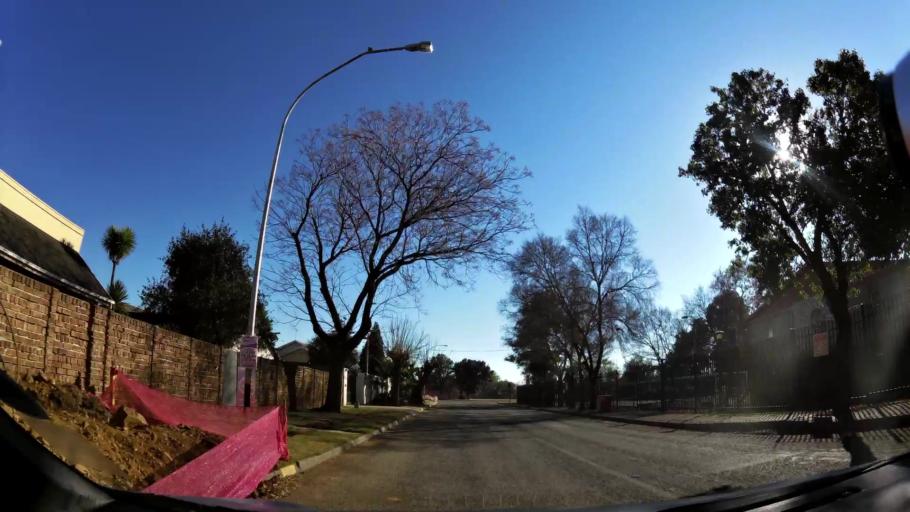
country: ZA
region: Gauteng
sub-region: Ekurhuleni Metropolitan Municipality
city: Germiston
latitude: -26.2823
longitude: 28.1138
